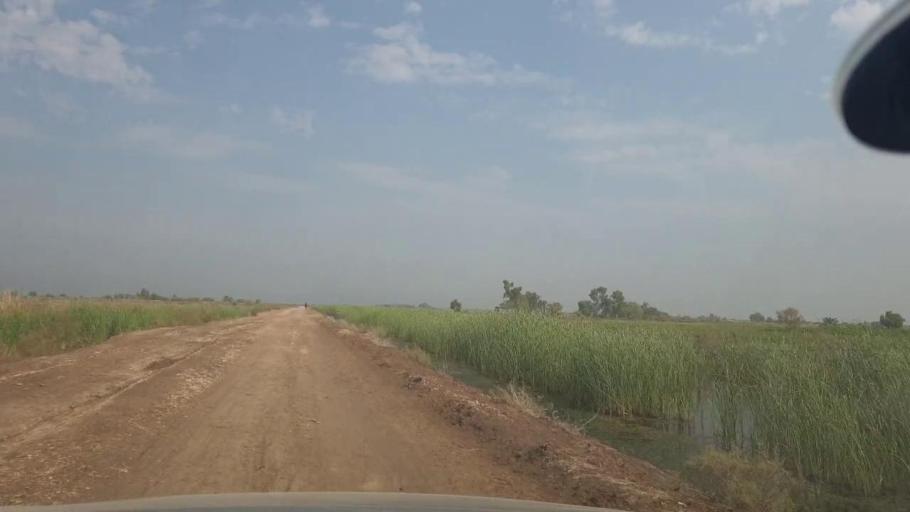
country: PK
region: Balochistan
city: Mehrabpur
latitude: 28.0277
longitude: 68.1325
